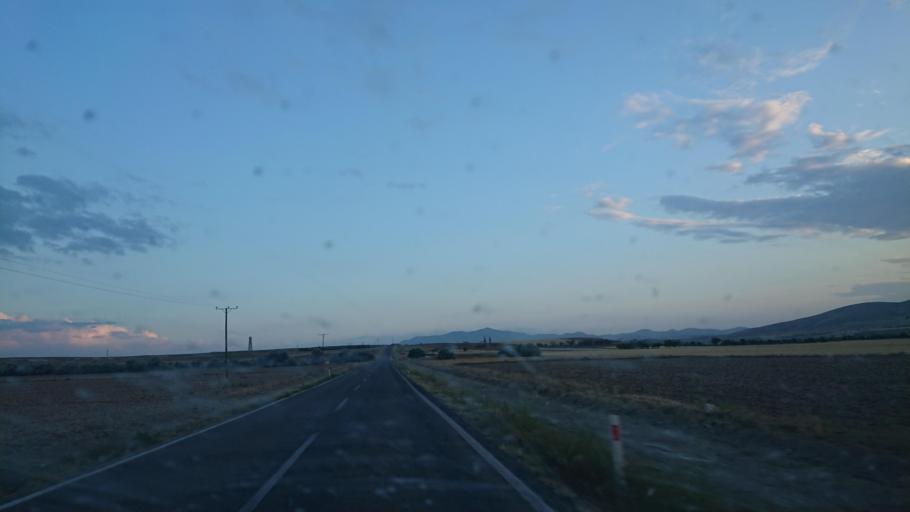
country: TR
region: Aksaray
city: Balci
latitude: 38.8075
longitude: 34.1314
